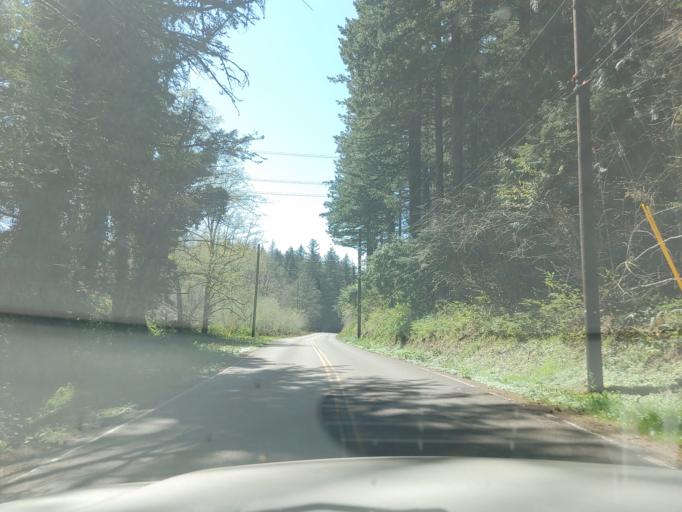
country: US
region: Washington
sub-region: Clark County
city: Washougal
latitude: 45.5223
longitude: -122.3196
